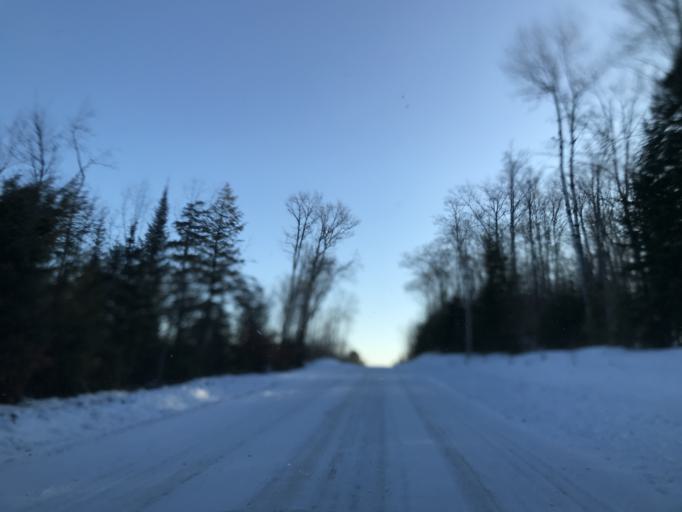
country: US
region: Michigan
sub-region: Menominee County
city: Menominee
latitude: 45.2906
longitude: -87.7041
